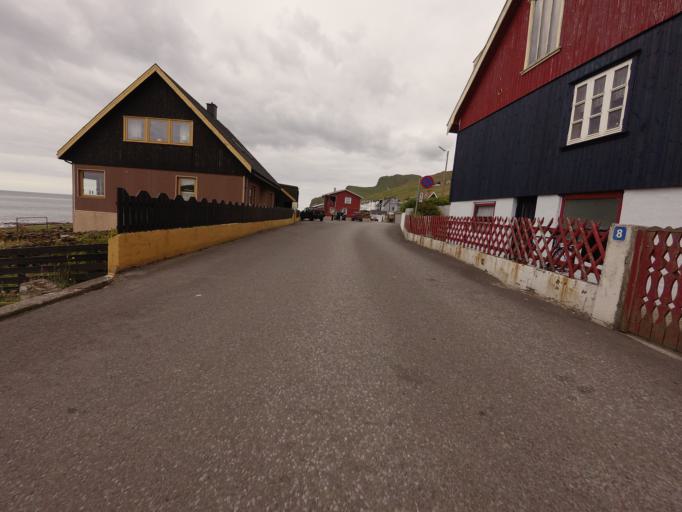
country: FO
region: Suduroy
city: Vagur
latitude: 61.4043
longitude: -6.7169
